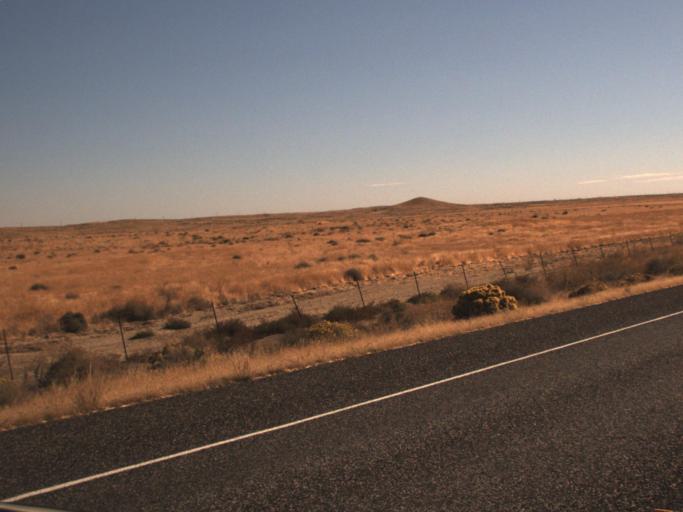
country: US
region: Washington
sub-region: Benton County
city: Benton City
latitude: 46.4905
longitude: -119.5913
